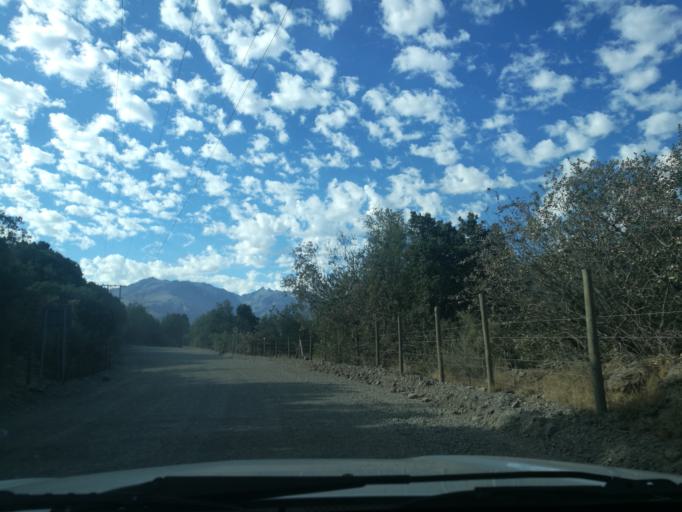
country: CL
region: O'Higgins
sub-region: Provincia de Cachapoal
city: Machali
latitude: -34.2869
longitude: -70.4380
